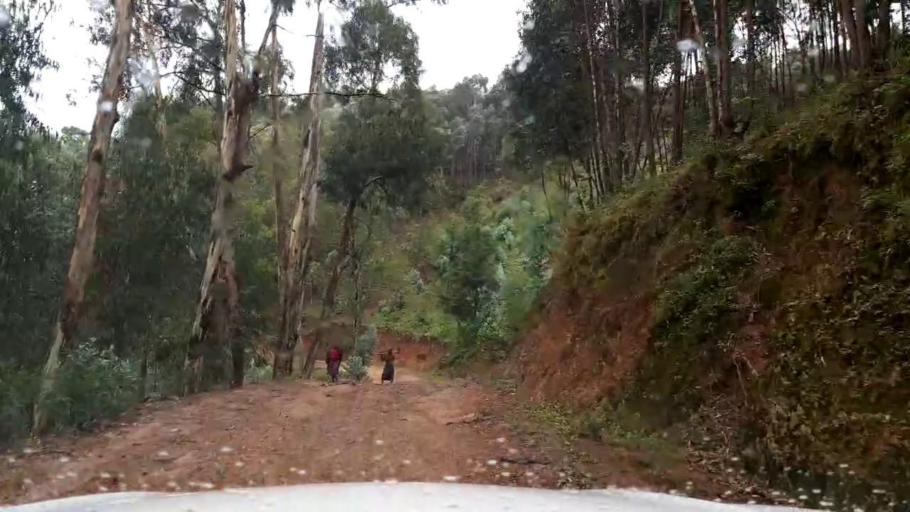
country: RW
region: Western Province
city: Kibuye
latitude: -2.0265
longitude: 29.4526
